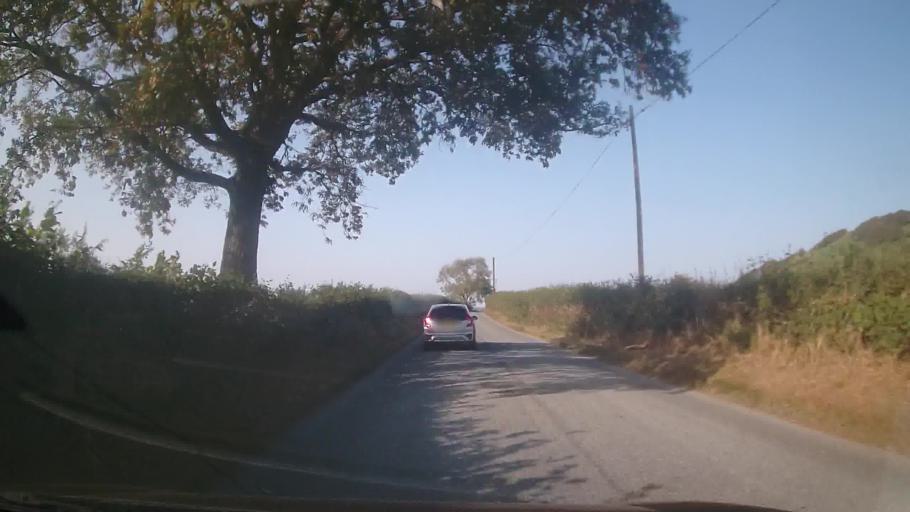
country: GB
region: Wales
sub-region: County of Ceredigion
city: Lledrod
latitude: 52.2310
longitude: -3.9314
